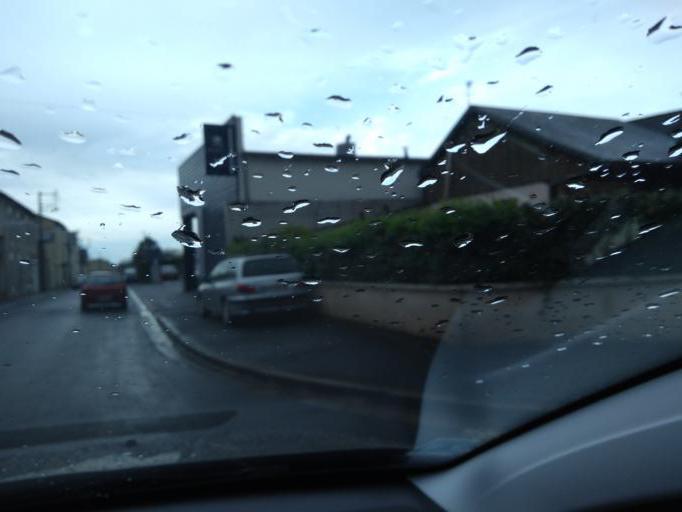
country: FR
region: Poitou-Charentes
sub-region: Departement de la Vienne
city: Loudun
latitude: 47.0050
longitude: 0.0821
